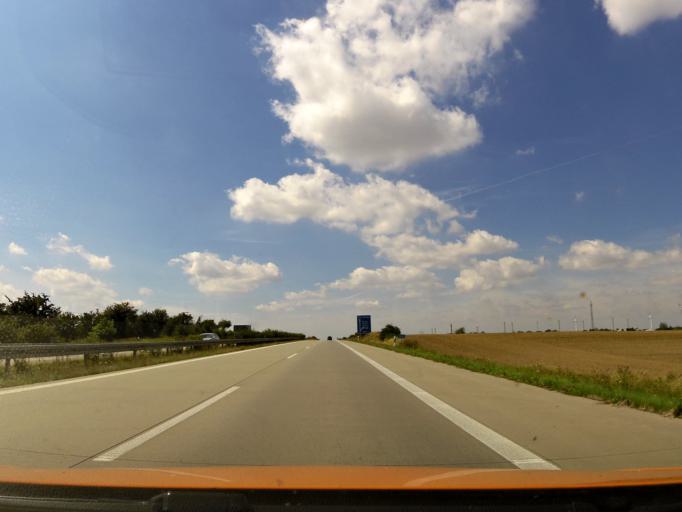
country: DE
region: Mecklenburg-Vorpommern
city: Penkun
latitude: 53.3178
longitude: 14.2863
